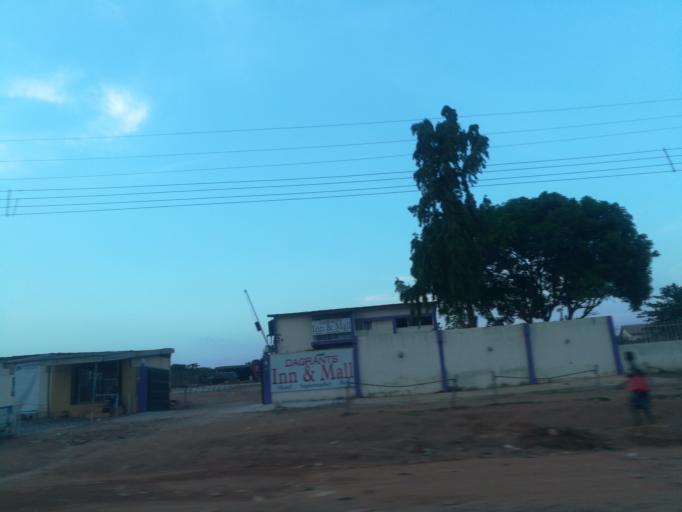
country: NG
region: Ogun
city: Abeokuta
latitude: 7.1775
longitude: 3.3915
